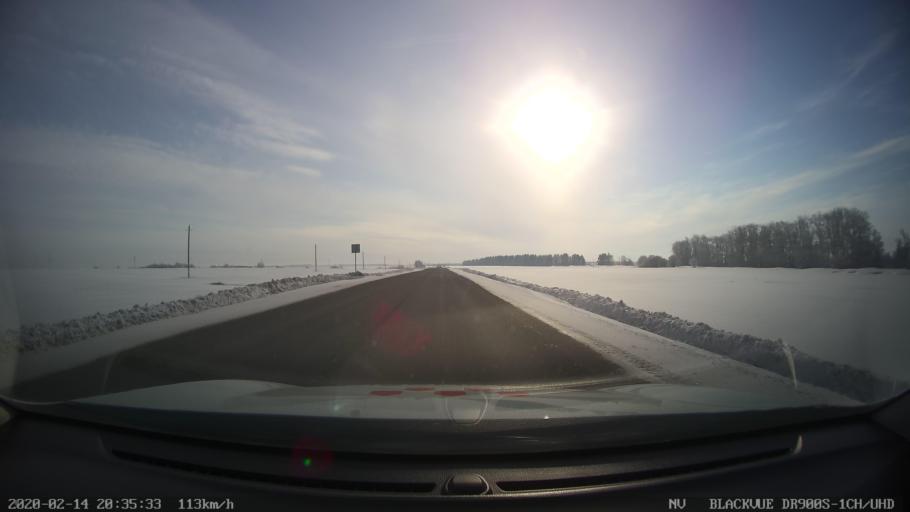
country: RU
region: Tatarstan
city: Kuybyshevskiy Zaton
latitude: 55.3807
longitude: 48.9859
